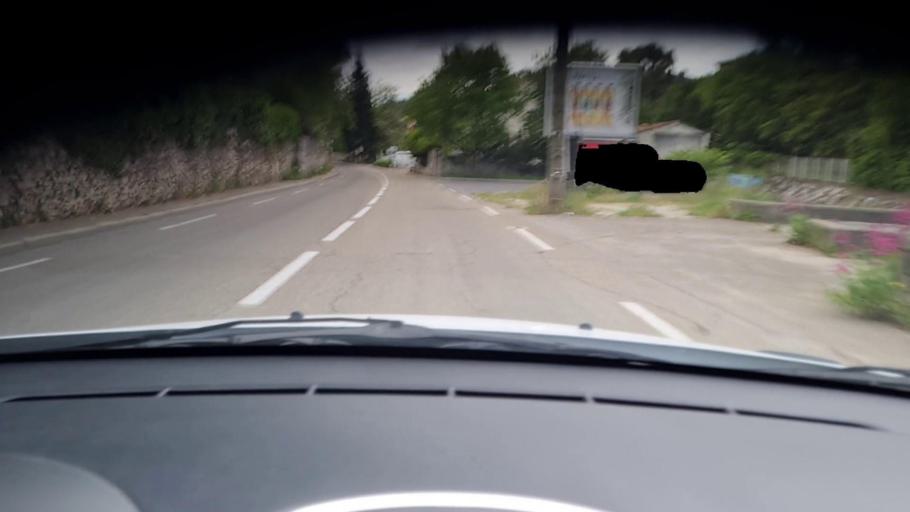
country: FR
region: Languedoc-Roussillon
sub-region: Departement du Gard
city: Nimes
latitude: 43.8570
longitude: 4.3784
